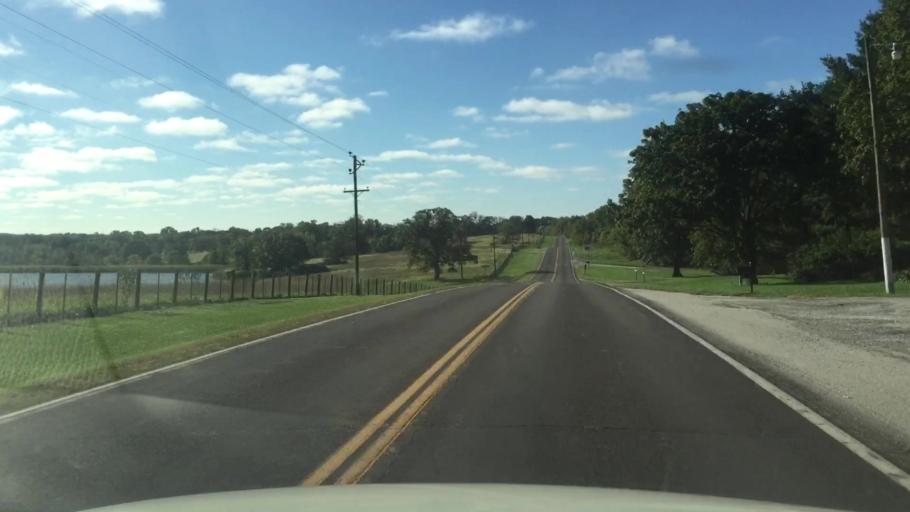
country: US
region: Missouri
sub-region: Howard County
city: New Franklin
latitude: 39.0456
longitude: -92.7444
